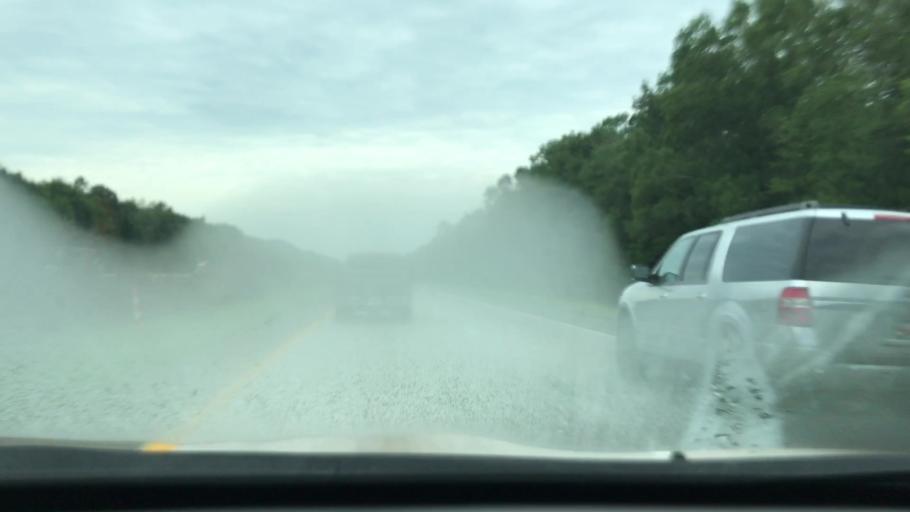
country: US
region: South Carolina
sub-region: Jasper County
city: Hardeeville
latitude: 32.3473
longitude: -81.0450
